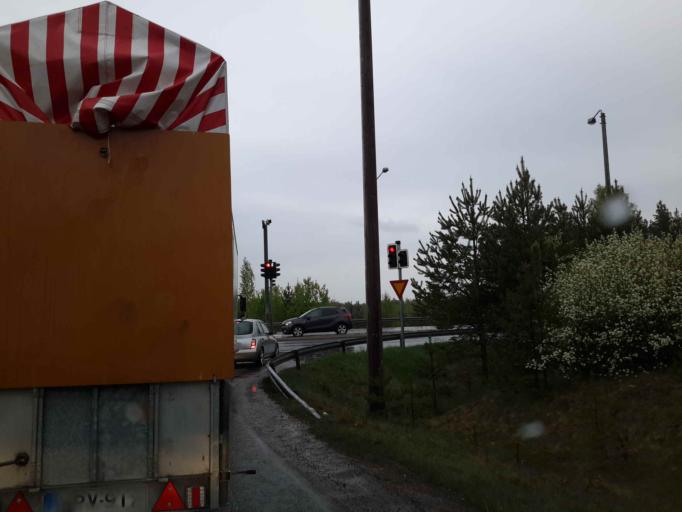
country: FI
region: Uusimaa
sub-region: Helsinki
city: Vihti
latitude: 60.3477
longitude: 24.3197
